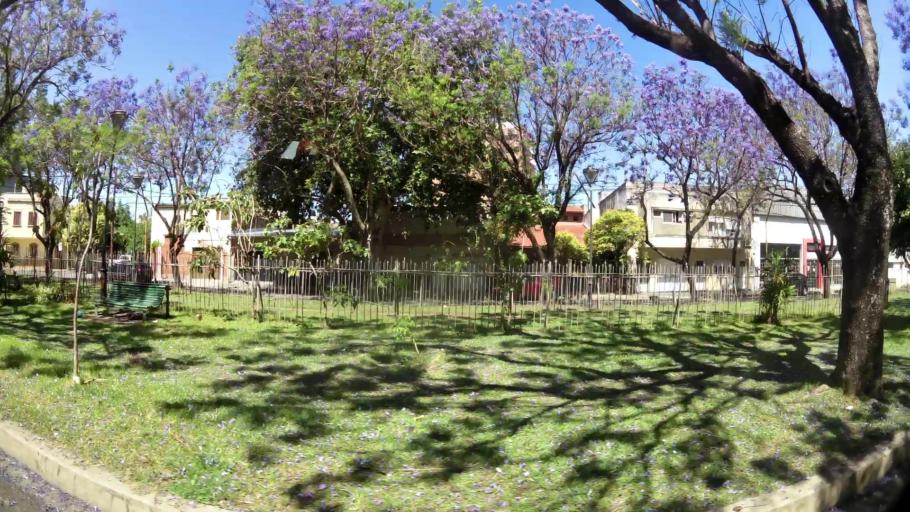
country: AR
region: Santa Fe
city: Santa Fe de la Vera Cruz
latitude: -31.6415
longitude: -60.6865
